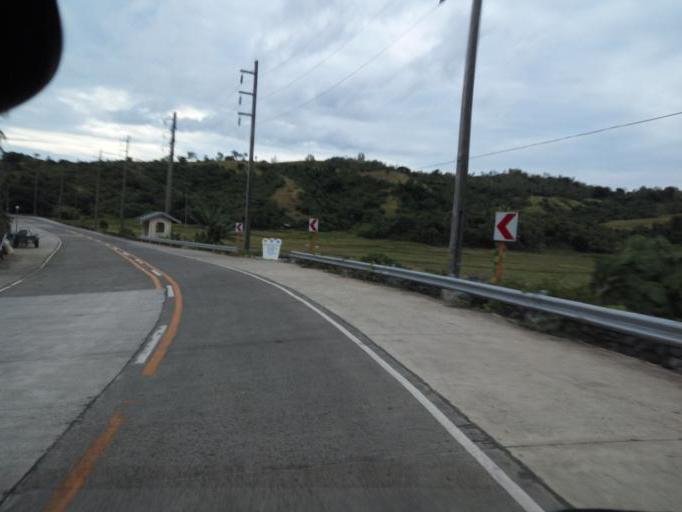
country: PH
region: Cagayan Valley
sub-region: Province of Cagayan
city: Casambalangan
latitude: 18.3924
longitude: 122.1387
